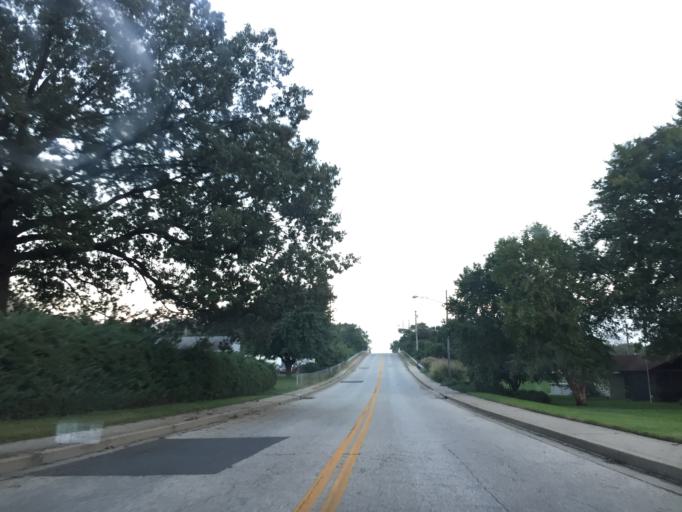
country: US
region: Maryland
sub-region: Baltimore County
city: Rosedale
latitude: 39.3118
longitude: -76.4988
